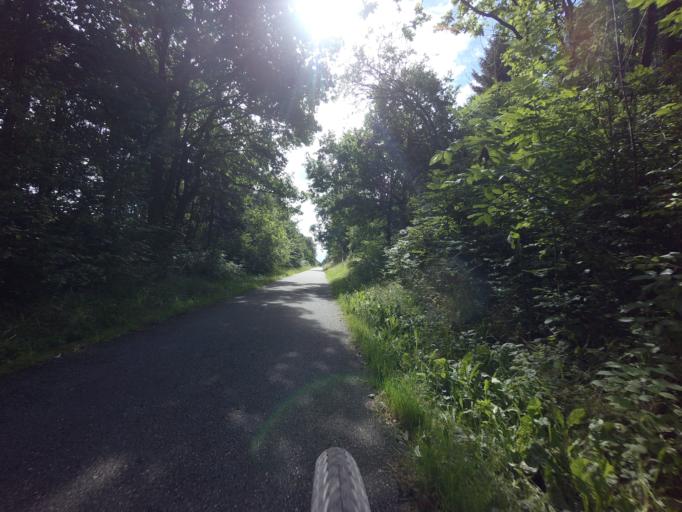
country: DK
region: Central Jutland
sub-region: Norddjurs Kommune
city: Auning
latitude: 56.4459
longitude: 10.3634
